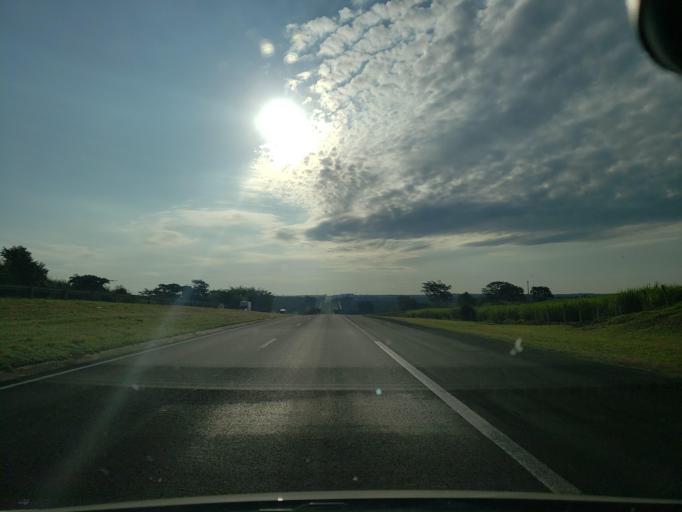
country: BR
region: Sao Paulo
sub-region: Valparaiso
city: Valparaiso
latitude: -21.1919
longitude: -50.9069
